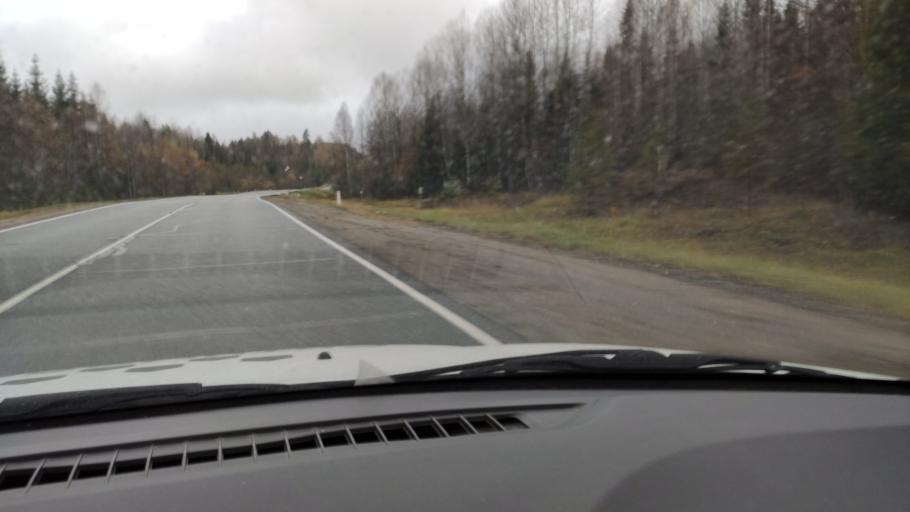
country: RU
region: Kirov
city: Chernaya Kholunitsa
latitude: 58.8916
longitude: 51.3441
